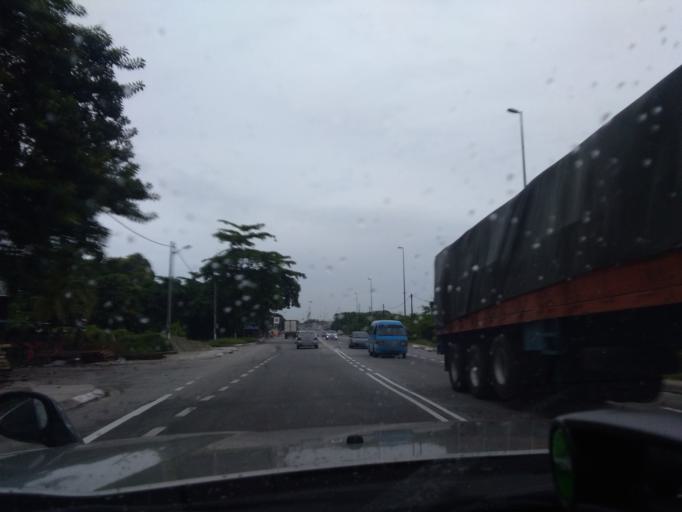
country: MY
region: Penang
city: Nibong Tebal
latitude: 5.1663
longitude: 100.4788
